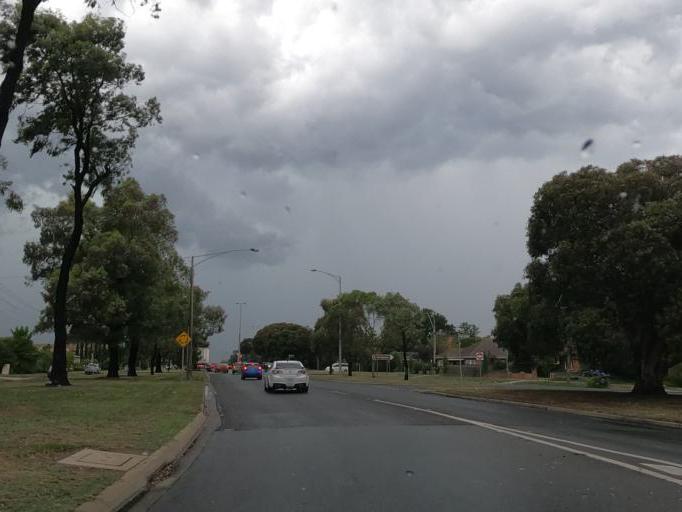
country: AU
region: Victoria
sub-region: Ballarat North
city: Newington
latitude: -37.5538
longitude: 143.8130
